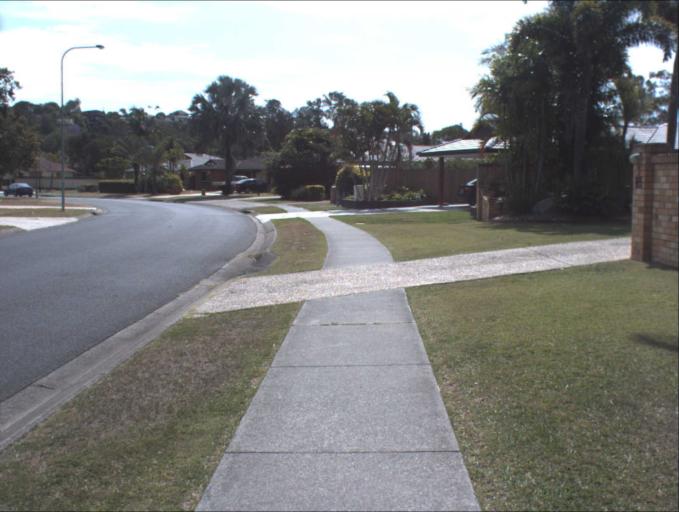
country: AU
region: Queensland
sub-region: Logan
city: Beenleigh
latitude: -27.6738
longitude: 153.2091
